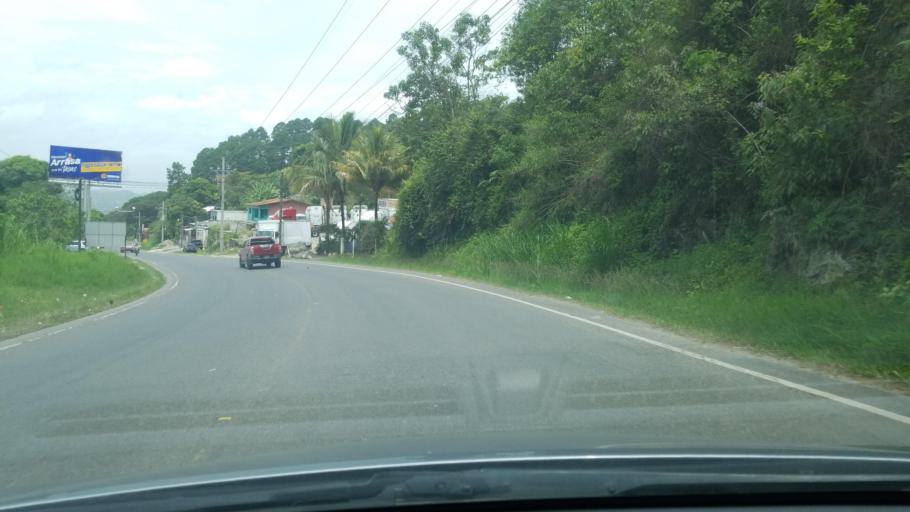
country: HN
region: Copan
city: Santa Rosa de Copan
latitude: 14.7546
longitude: -88.7773
